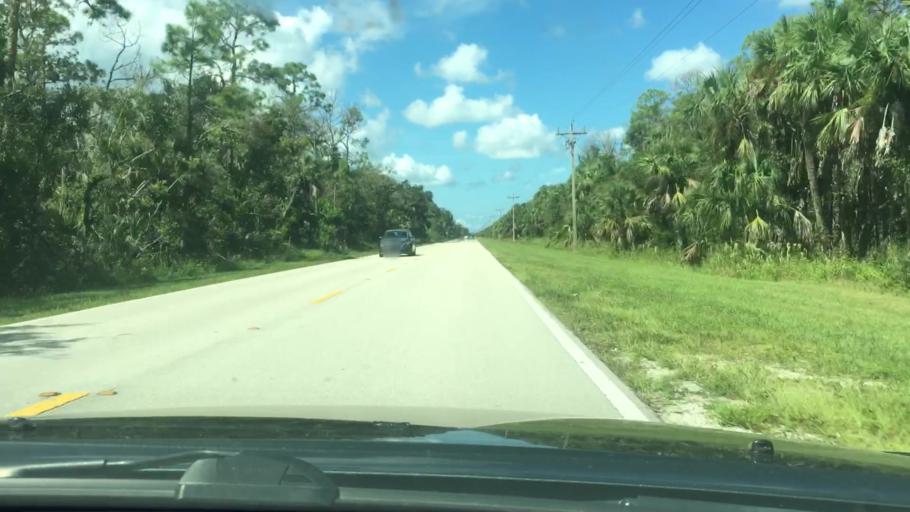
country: US
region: Florida
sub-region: Collier County
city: Lely Resort
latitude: 25.9937
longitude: -81.5943
